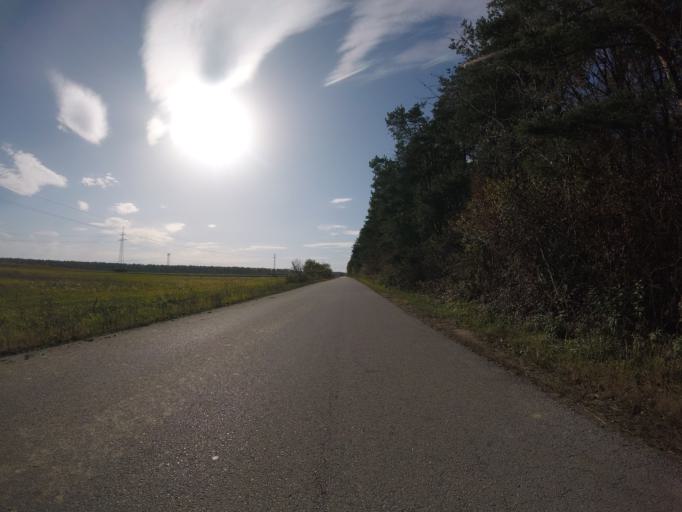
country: HR
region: Zagrebacka
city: Mraclin
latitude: 45.6537
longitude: 16.0719
